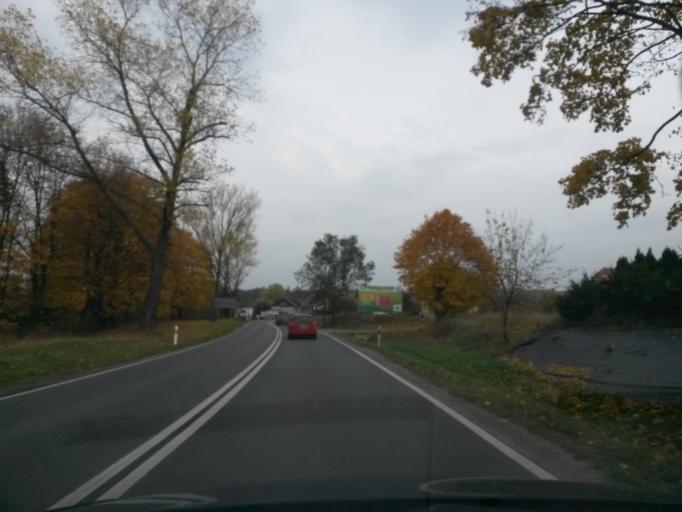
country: PL
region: Lower Silesian Voivodeship
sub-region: Powiat klodzki
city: Klodzko
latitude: 50.4180
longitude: 16.6604
